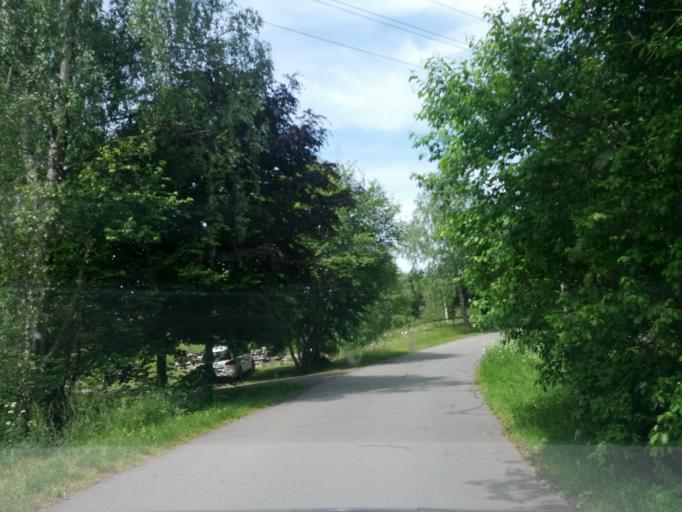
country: DE
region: Thuringia
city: Finsterbergen
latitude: 50.8384
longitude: 10.5852
